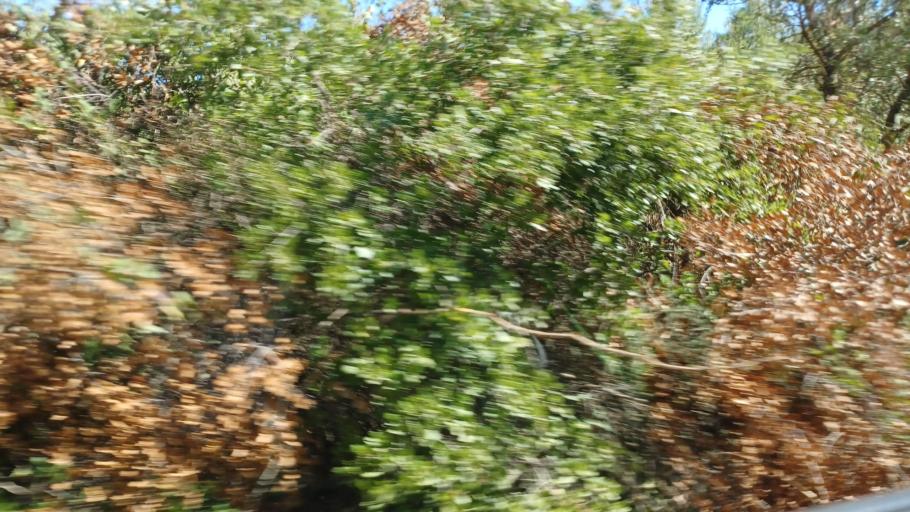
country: CY
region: Pafos
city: Mesogi
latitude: 34.9294
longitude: 32.6301
